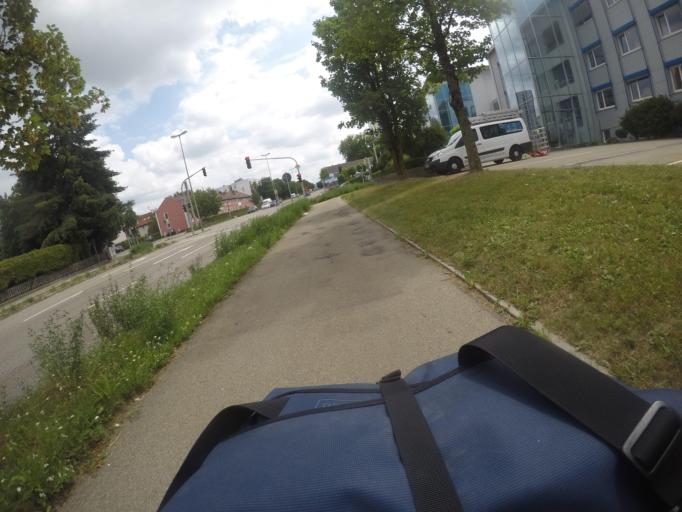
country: DE
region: Bavaria
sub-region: Swabia
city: Memmingen
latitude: 48.0018
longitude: 10.1745
